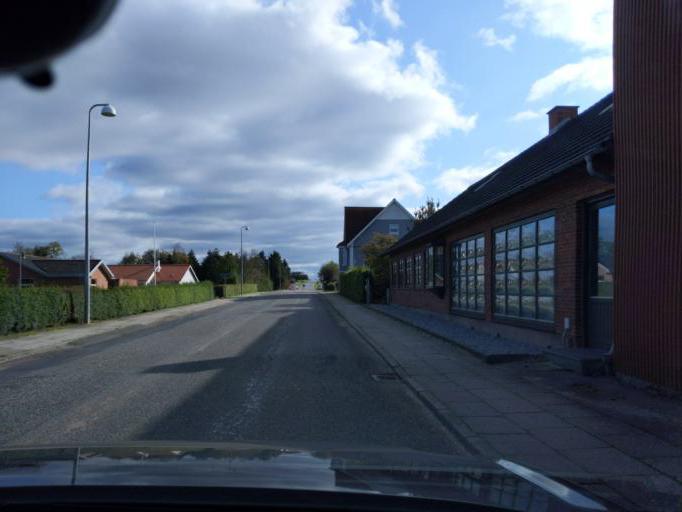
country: DK
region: North Denmark
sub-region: Mariagerfjord Kommune
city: Hobro
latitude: 56.5259
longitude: 9.7290
